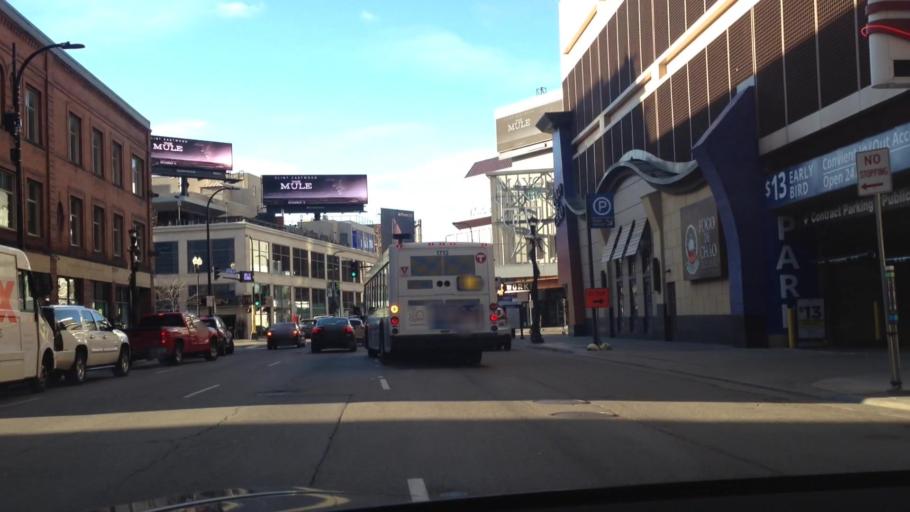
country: US
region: Minnesota
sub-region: Hennepin County
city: Minneapolis
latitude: 44.9777
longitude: -93.2740
